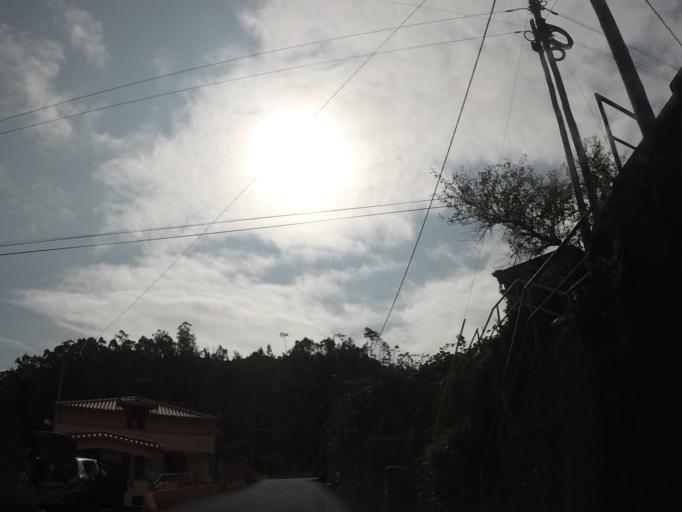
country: PT
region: Madeira
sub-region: Sao Vicente
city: Sao Vicente
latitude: 32.7807
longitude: -17.0434
